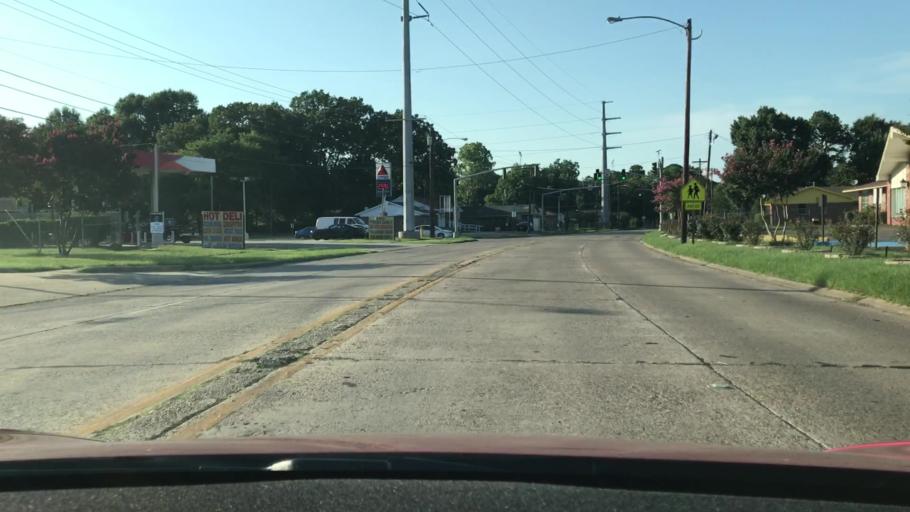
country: US
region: Louisiana
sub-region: Bossier Parish
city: Bossier City
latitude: 32.4321
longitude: -93.7458
